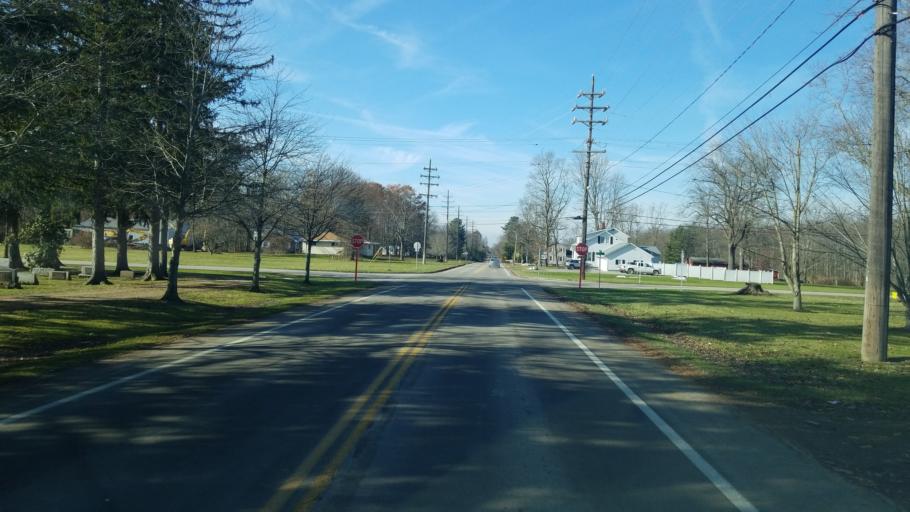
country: US
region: Ohio
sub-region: Ashtabula County
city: Jefferson
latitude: 41.7465
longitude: -80.7632
